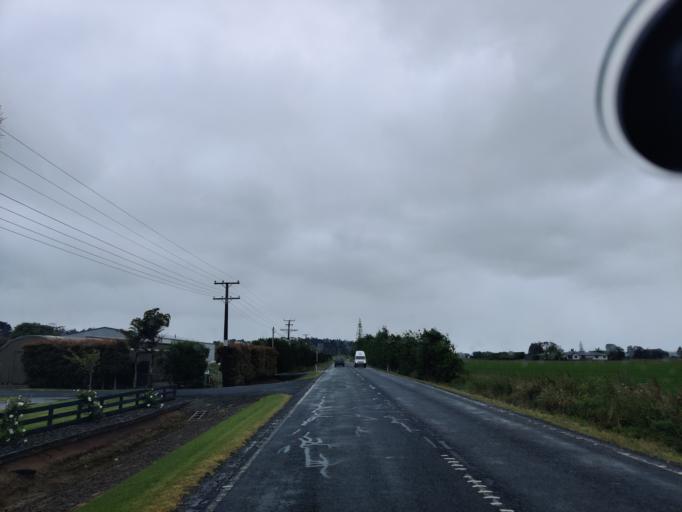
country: NZ
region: Northland
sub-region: Kaipara District
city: Dargaville
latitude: -35.9871
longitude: 173.9153
